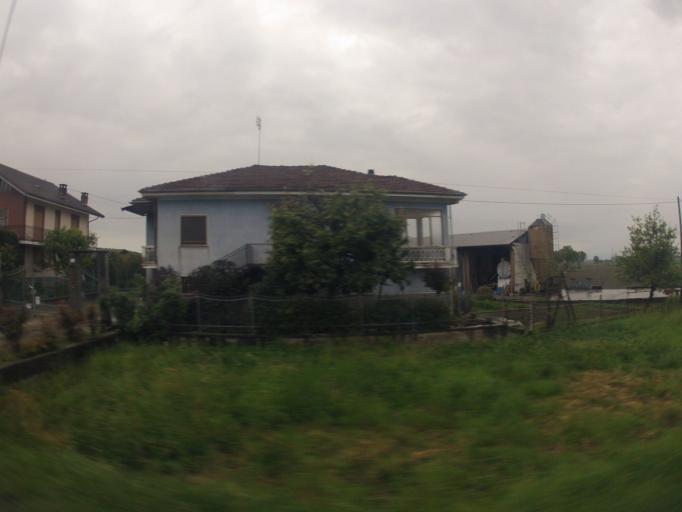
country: IT
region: Piedmont
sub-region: Provincia di Cuneo
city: Moretta
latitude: 44.7699
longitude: 7.5455
